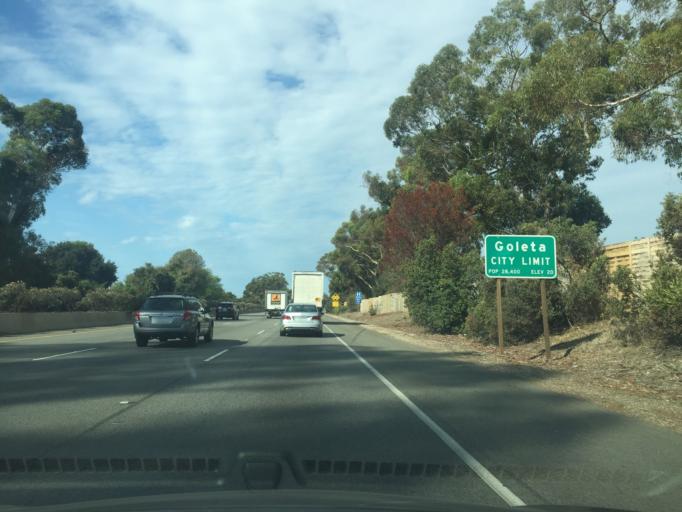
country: US
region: California
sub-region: Santa Barbara County
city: Goleta
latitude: 34.4417
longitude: -119.8001
